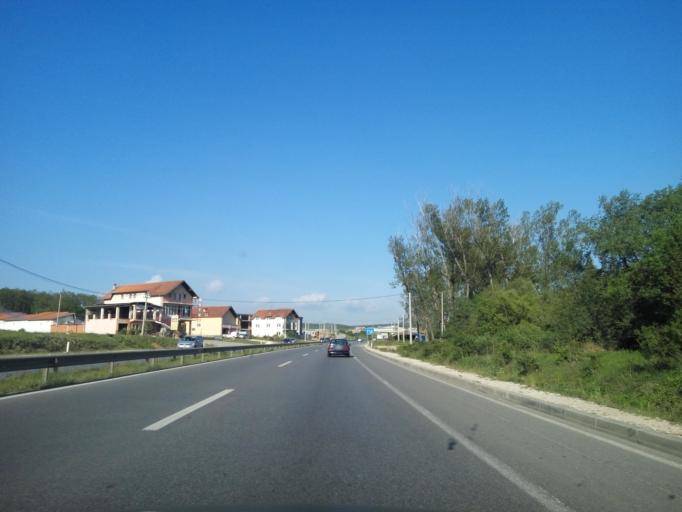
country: XK
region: Pristina
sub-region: Komuna e Drenasit
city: Glogovac
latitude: 42.6022
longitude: 20.9466
